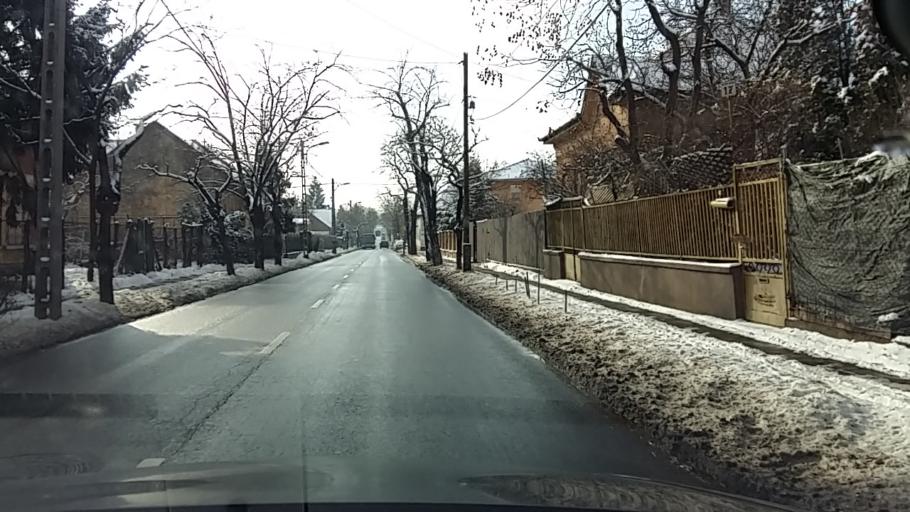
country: HU
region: Budapest
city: Budapest XVIII. keruelet
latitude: 47.4365
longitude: 19.1836
